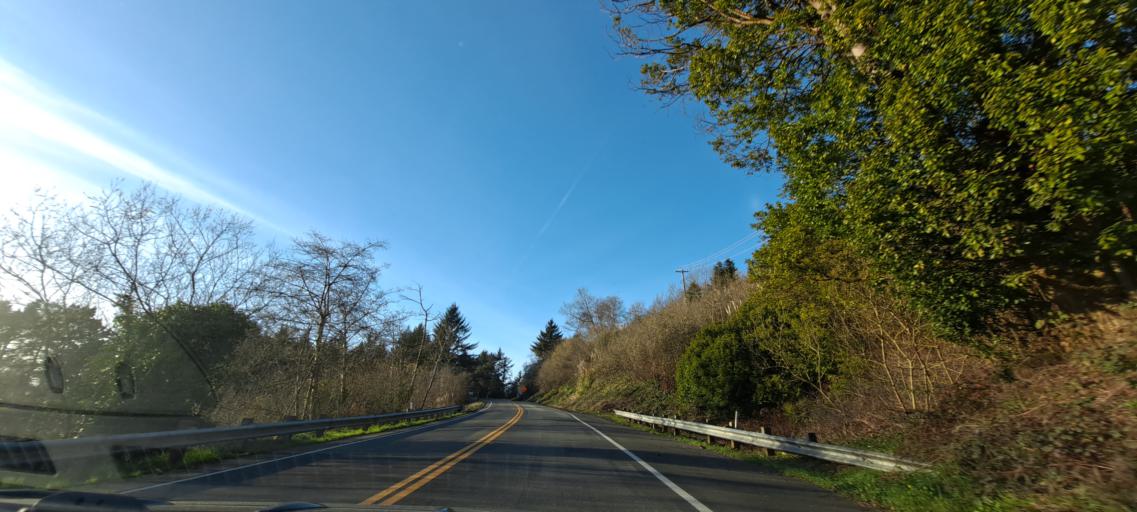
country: US
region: California
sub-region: Humboldt County
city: McKinleyville
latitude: 40.9214
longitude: -124.0966
